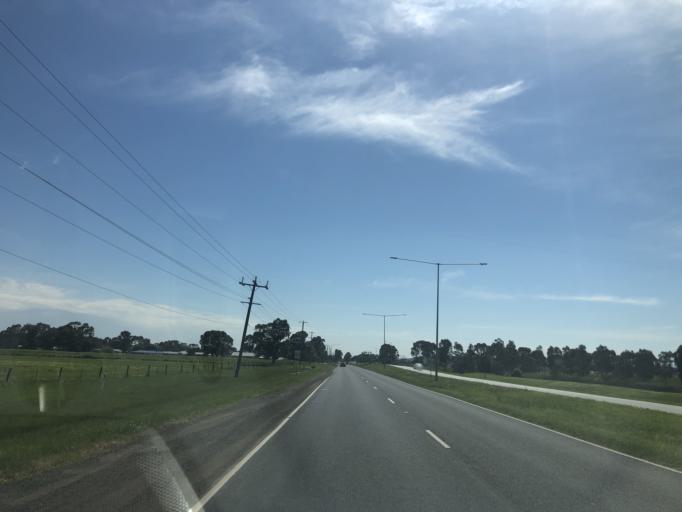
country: AU
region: Victoria
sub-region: Frankston
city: Sandhurst
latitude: -38.0465
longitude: 145.2090
